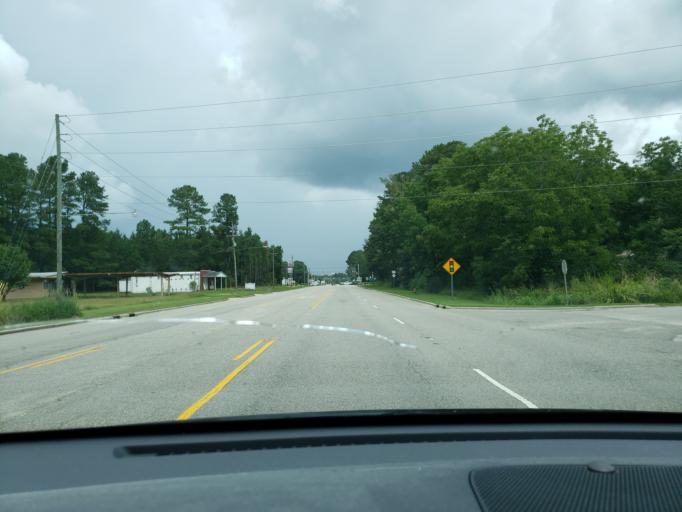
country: US
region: North Carolina
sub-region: Bladen County
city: Bladenboro
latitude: 34.4875
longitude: -78.6630
